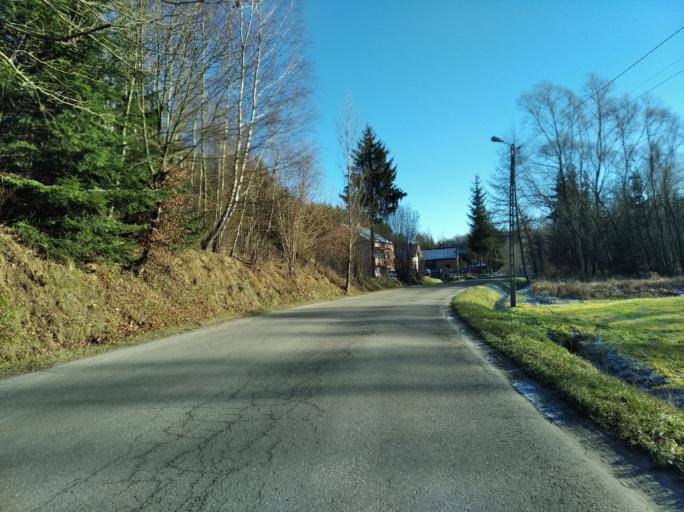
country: PL
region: Subcarpathian Voivodeship
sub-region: Powiat strzyzowski
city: Strzyzow
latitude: 49.9250
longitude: 21.7869
